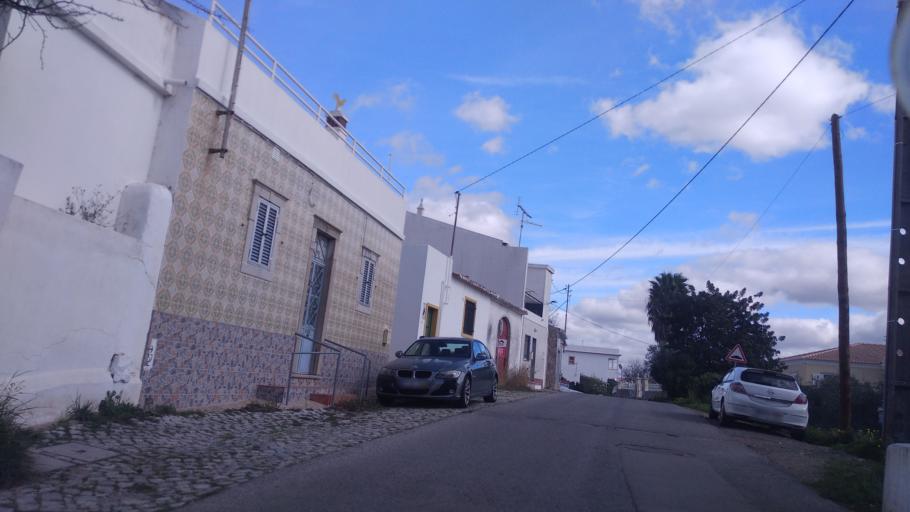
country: PT
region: Faro
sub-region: Sao Bras de Alportel
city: Sao Bras de Alportel
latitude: 37.1493
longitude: -7.8993
